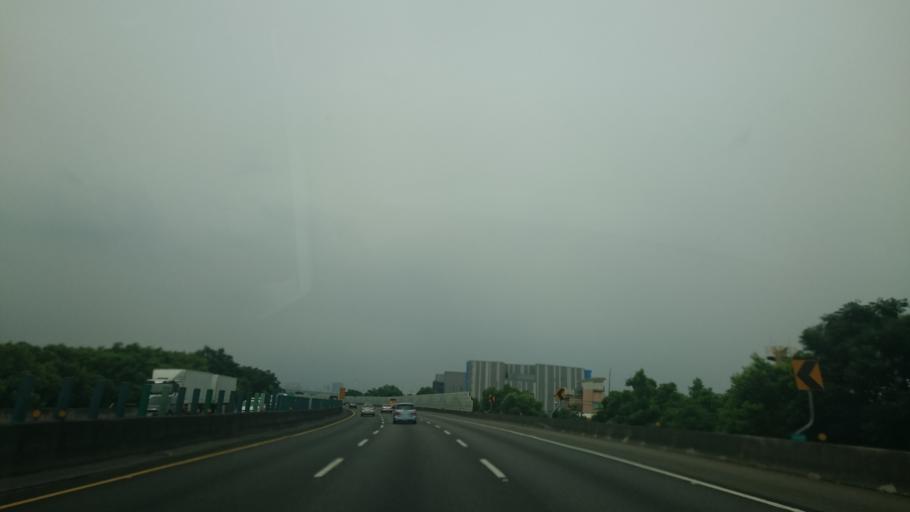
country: TW
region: Taiwan
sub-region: Changhua
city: Chang-hua
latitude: 24.1117
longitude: 120.6041
